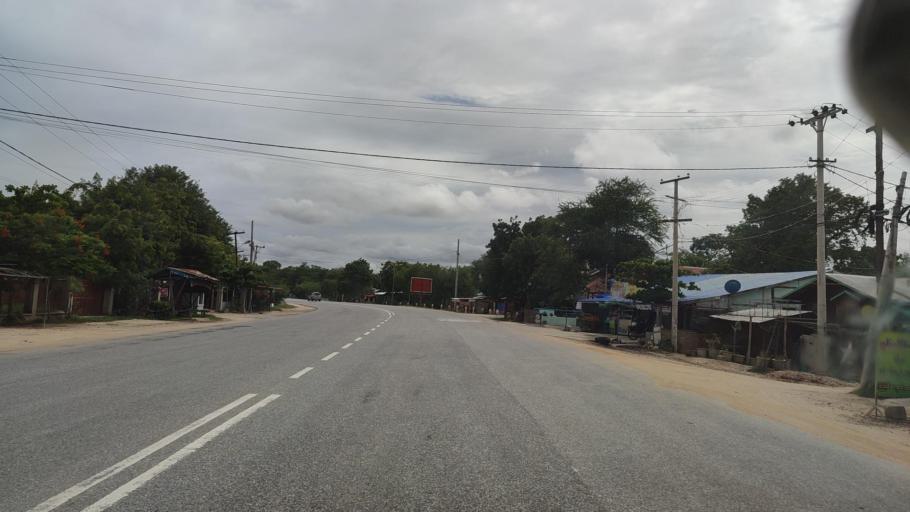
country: MM
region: Mandalay
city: Meiktila
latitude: 21.0497
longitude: 95.9973
